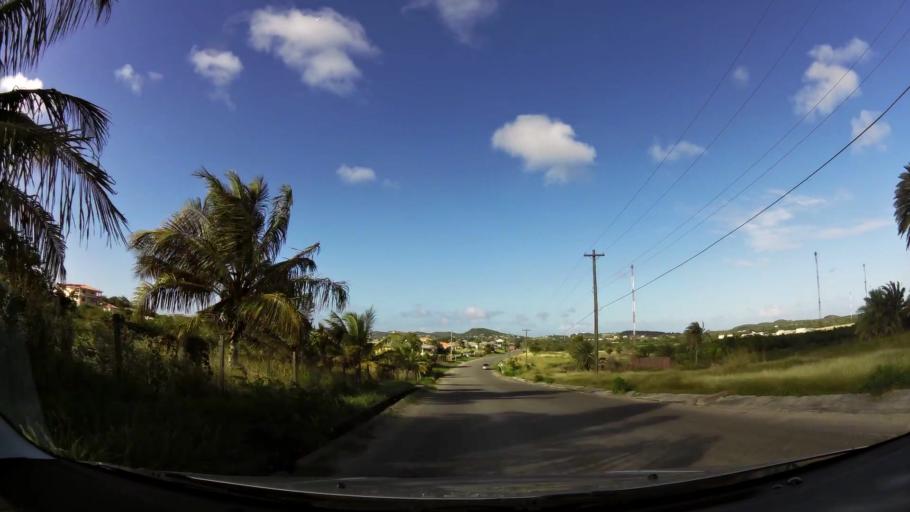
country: AG
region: Saint George
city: Piggotts
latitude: 17.0967
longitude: -61.8016
